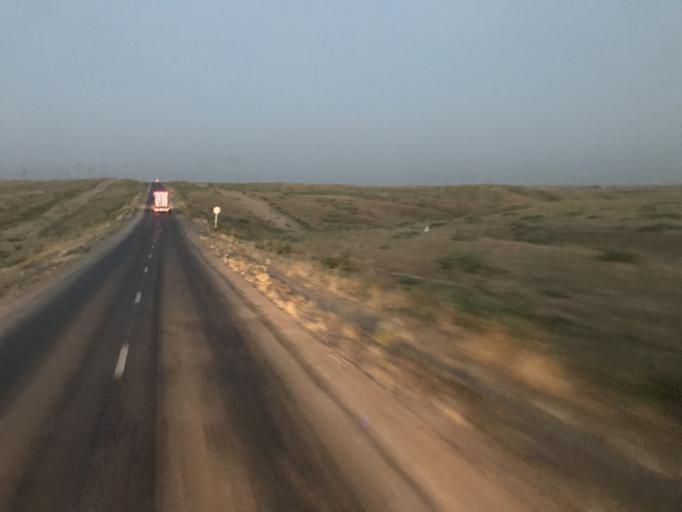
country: UZ
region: Toshkent
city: Chinoz
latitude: 41.1399
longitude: 68.7050
